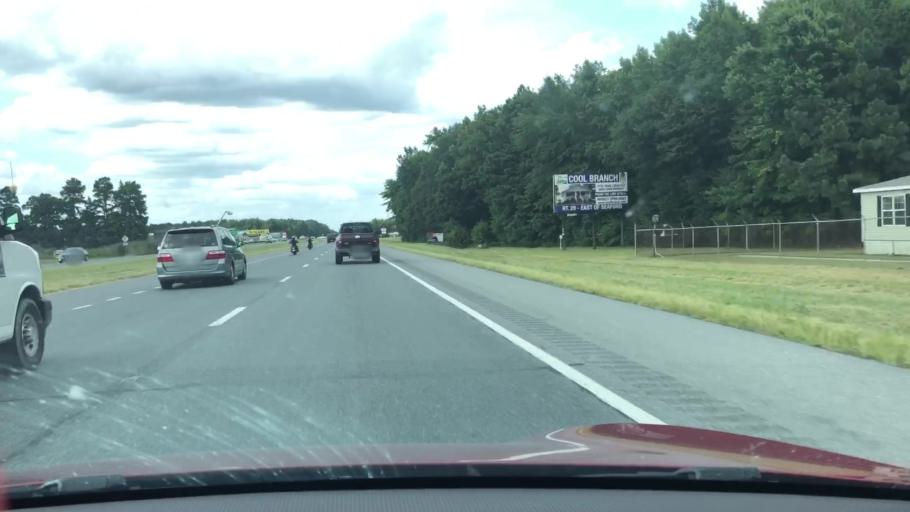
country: US
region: Delaware
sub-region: Sussex County
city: Delmar
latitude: 38.4797
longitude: -75.5576
